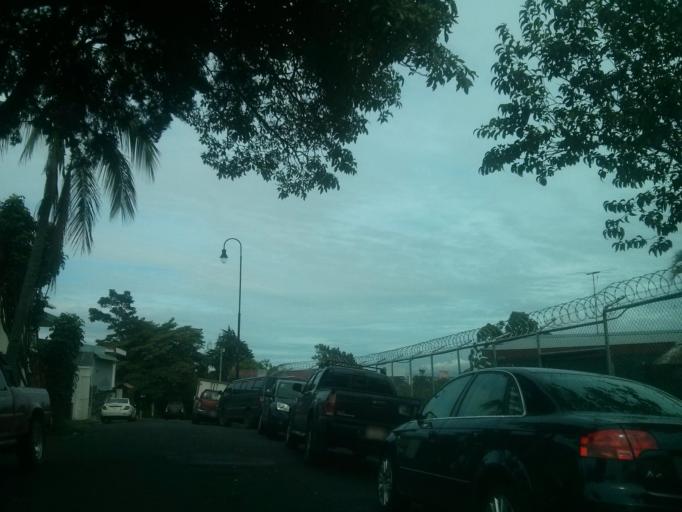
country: CR
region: San Jose
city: Calle Blancos
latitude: 9.9395
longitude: -84.0669
